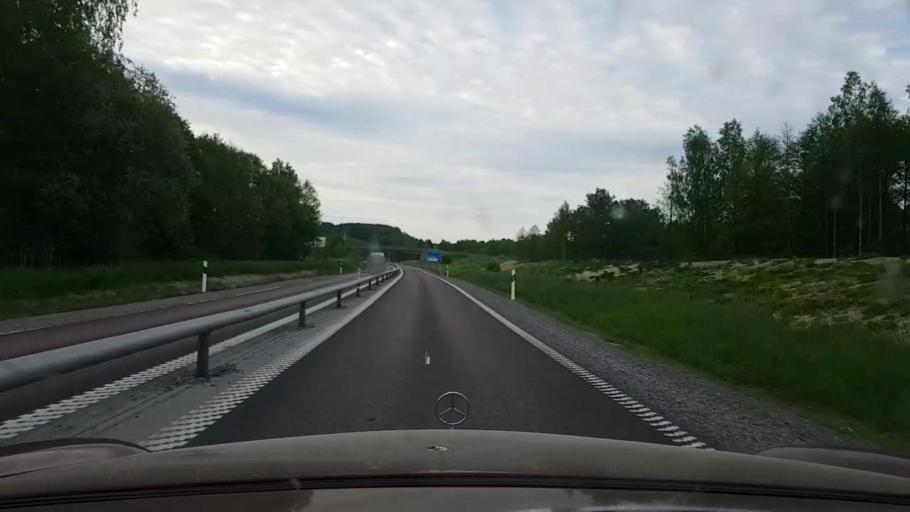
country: SE
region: OErebro
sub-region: Askersunds Kommun
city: Askersund
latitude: 58.8834
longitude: 14.8983
